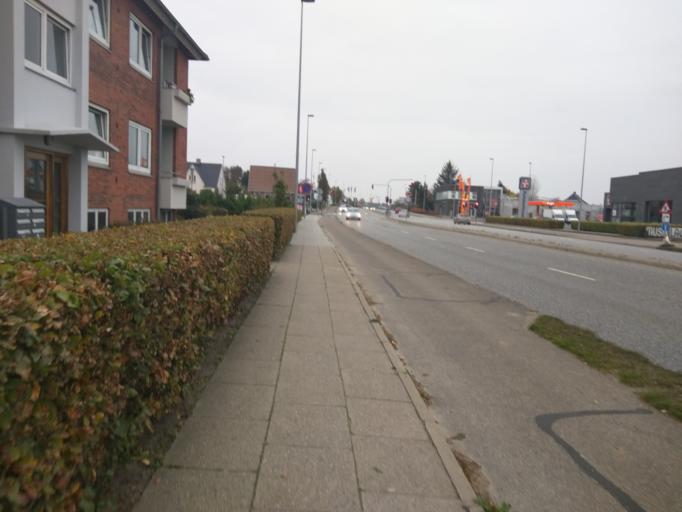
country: DK
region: Central Jutland
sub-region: Viborg Kommune
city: Viborg
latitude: 56.4535
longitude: 9.3925
